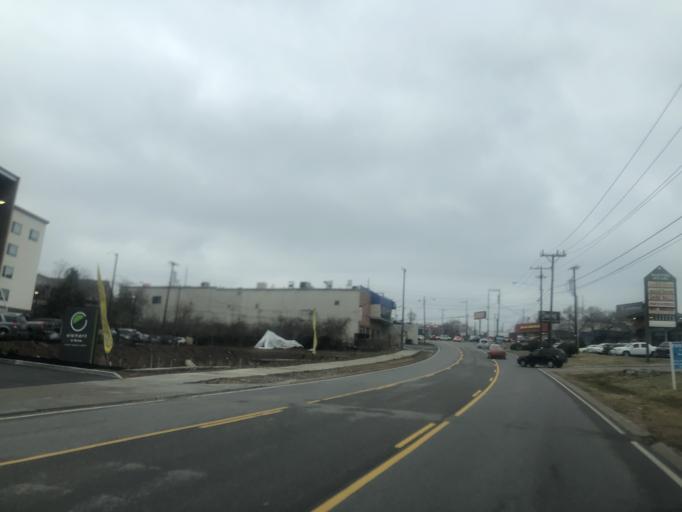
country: US
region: Tennessee
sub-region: Davidson County
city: Lakewood
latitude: 36.1481
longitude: -86.6640
